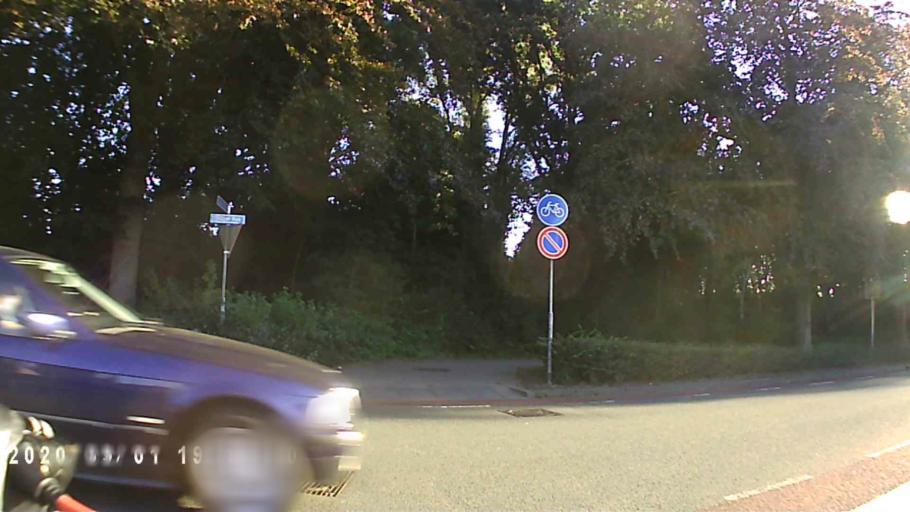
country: NL
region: Groningen
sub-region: Gemeente Veendam
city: Veendam
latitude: 53.0966
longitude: 6.8672
